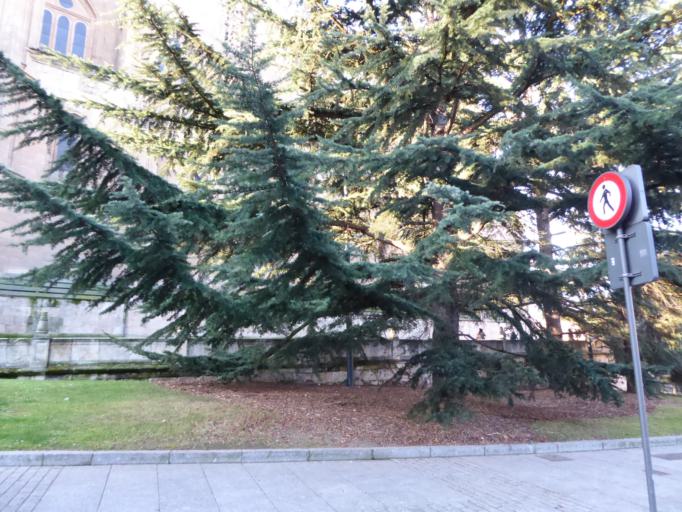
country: ES
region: Castille and Leon
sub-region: Provincia de Salamanca
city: Salamanca
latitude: 40.9610
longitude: -5.6627
